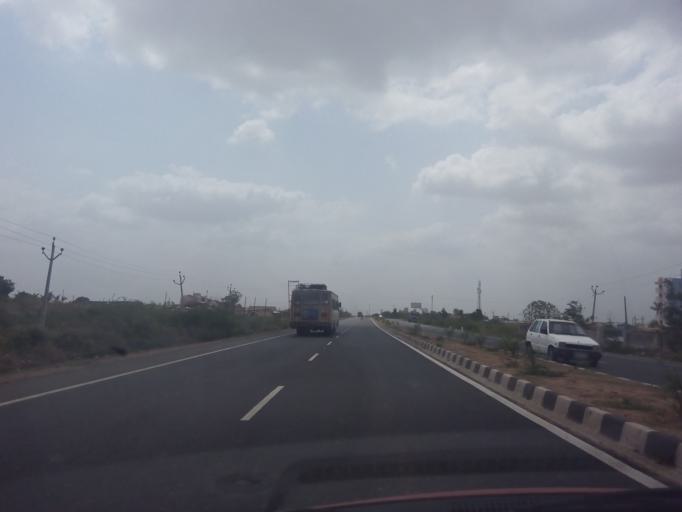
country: IN
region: Gujarat
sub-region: Surendranagar
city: Dhrangadhra
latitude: 22.9997
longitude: 71.4211
